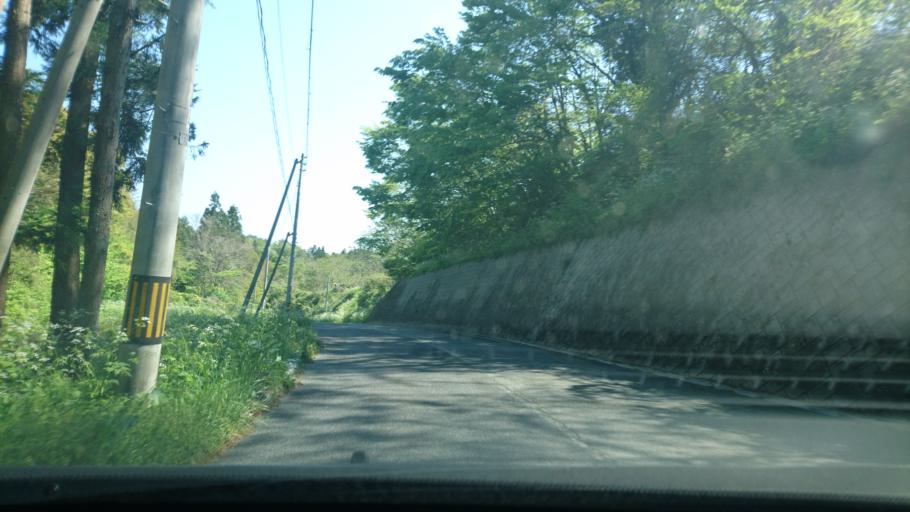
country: JP
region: Iwate
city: Ichinoseki
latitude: 38.9163
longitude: 141.2784
